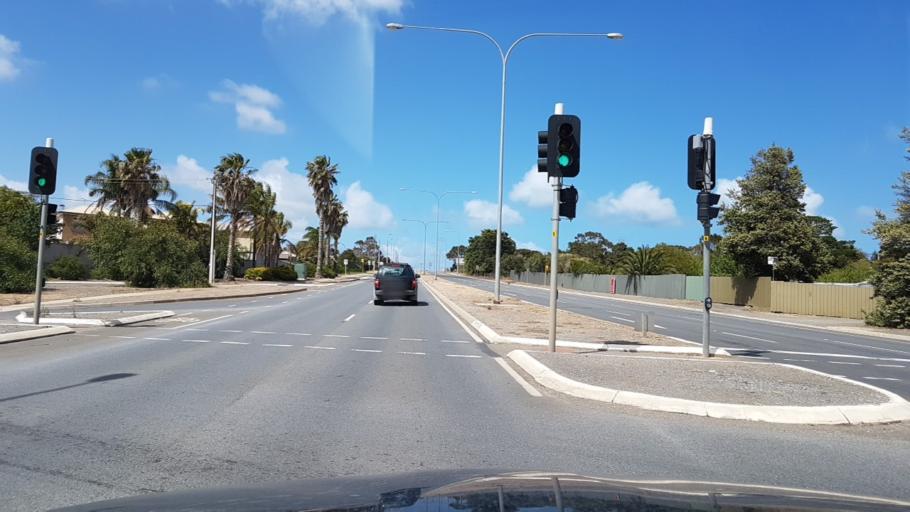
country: AU
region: South Australia
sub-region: Onkaparinga
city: Noarlunga
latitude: -35.1828
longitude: 138.4940
